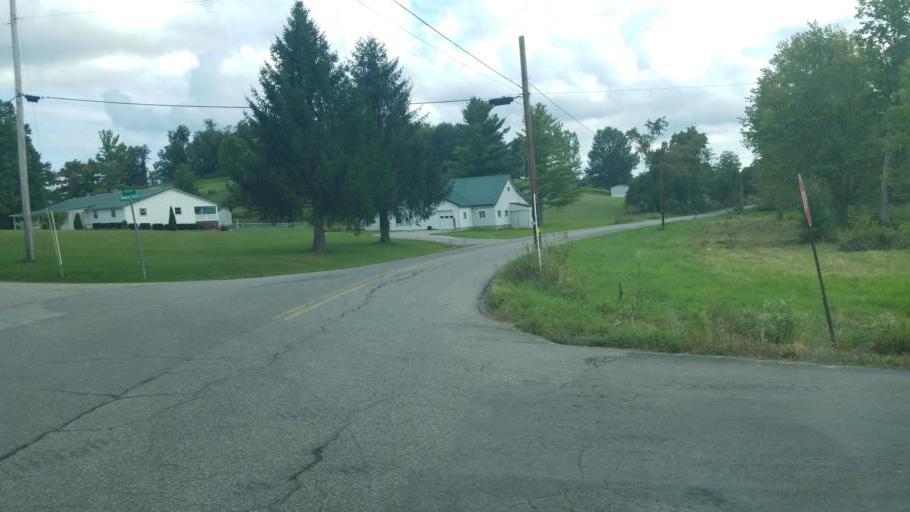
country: US
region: Ohio
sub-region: Jackson County
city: Oak Hill
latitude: 38.9278
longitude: -82.6041
